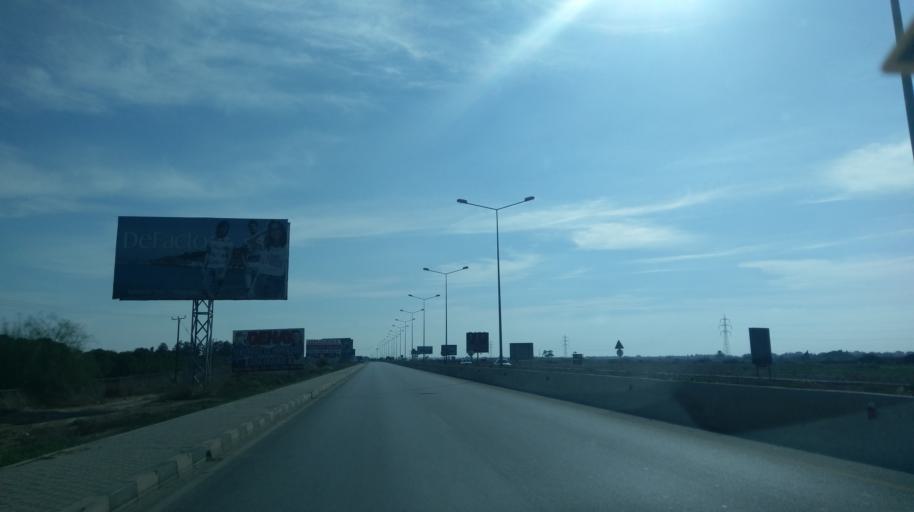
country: CY
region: Ammochostos
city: Famagusta
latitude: 35.1836
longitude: 33.8949
